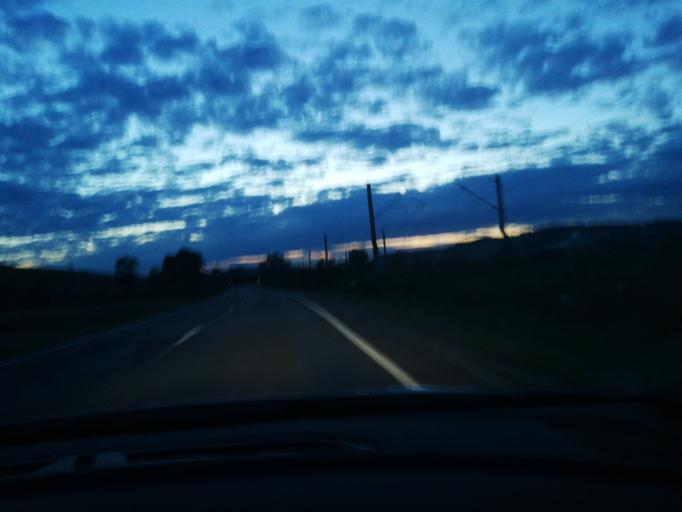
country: RO
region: Mures
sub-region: Comuna Vanatori
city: Vanatori
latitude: 46.2339
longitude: 24.9709
